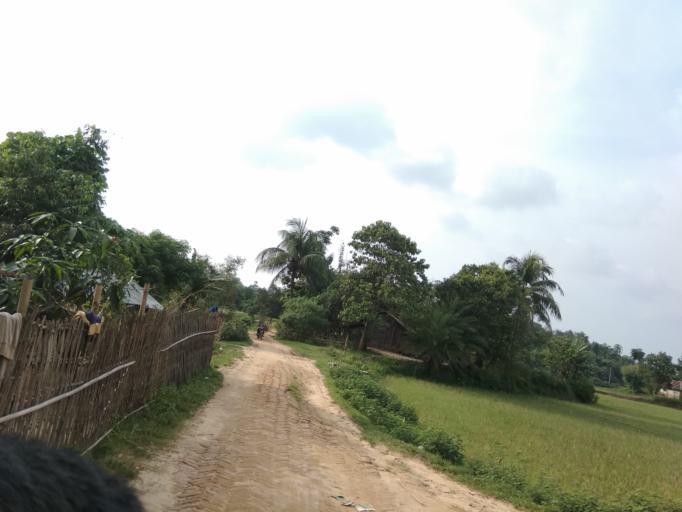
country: BD
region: Chittagong
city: Manikchari
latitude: 22.9326
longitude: 91.9106
